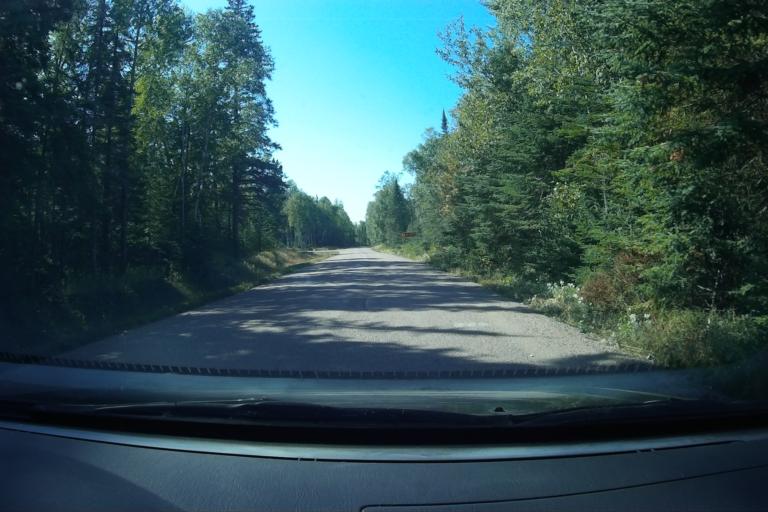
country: CA
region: Ontario
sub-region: Thunder Bay District
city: Thunder Bay
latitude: 48.3426
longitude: -88.7983
